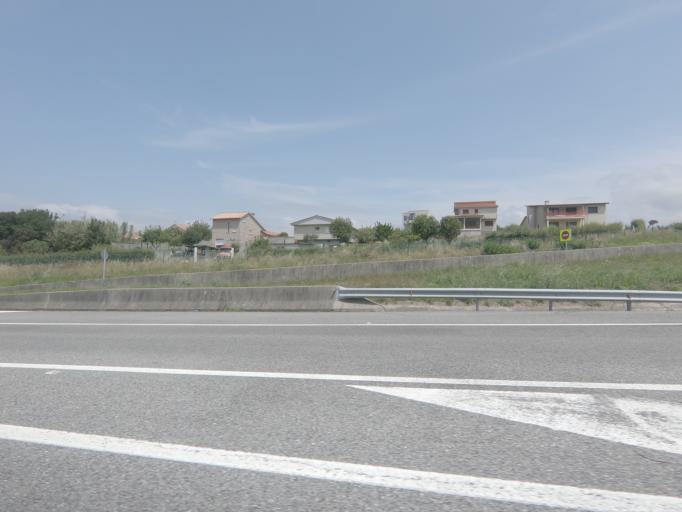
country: ES
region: Galicia
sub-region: Provincia de Pontevedra
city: Baiona
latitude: 42.1011
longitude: -8.8247
